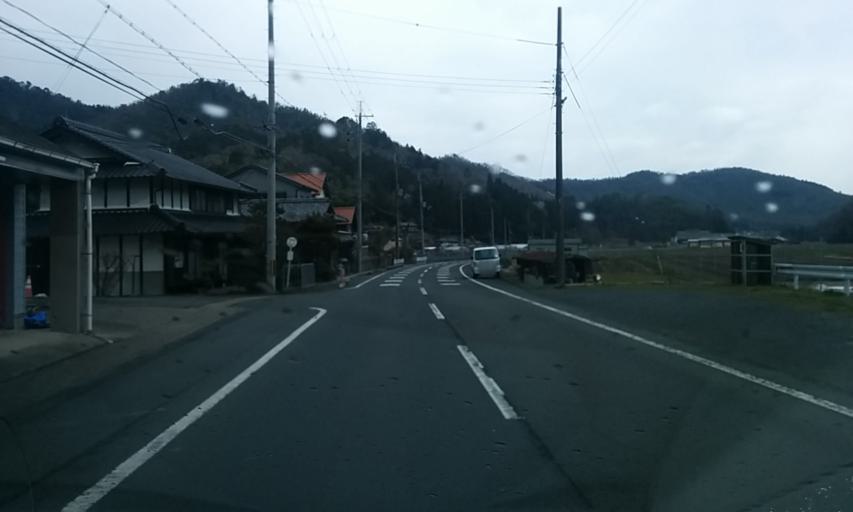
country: JP
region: Hyogo
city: Sasayama
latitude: 35.1291
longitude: 135.4117
